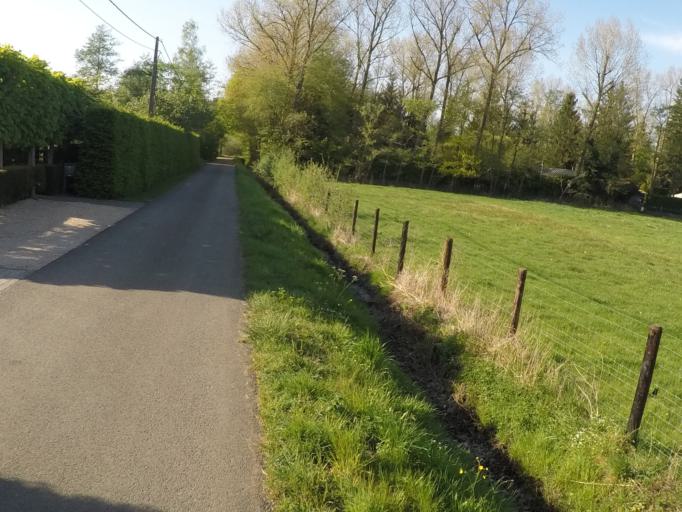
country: BE
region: Flanders
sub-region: Provincie Antwerpen
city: Nijlen
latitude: 51.1586
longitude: 4.6187
